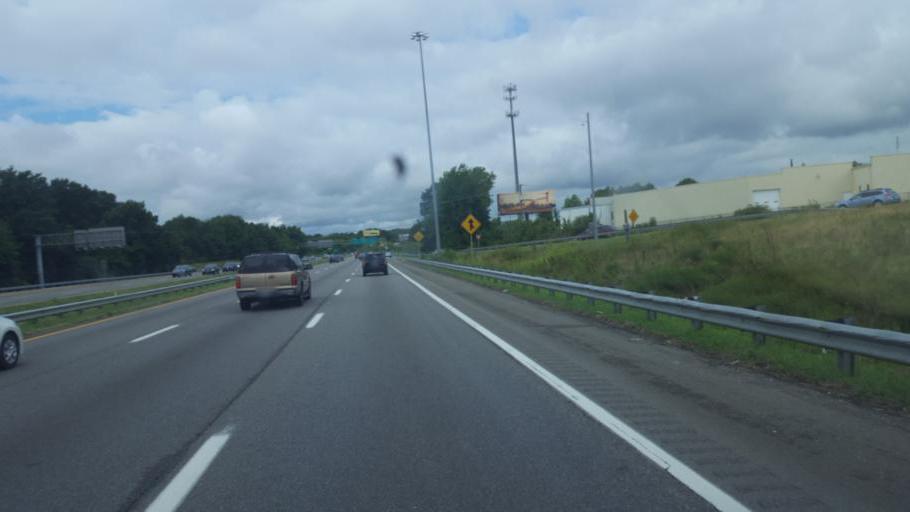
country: US
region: Virginia
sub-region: Henrico County
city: East Highland Park
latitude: 37.5565
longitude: -77.4108
